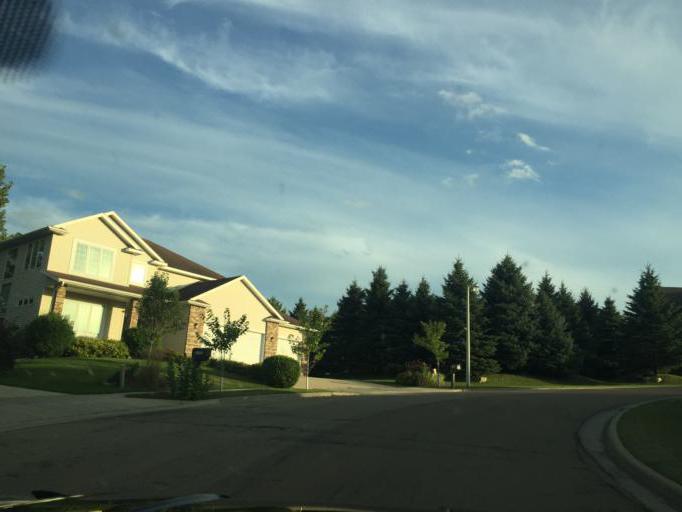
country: US
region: Minnesota
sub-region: Olmsted County
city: Rochester
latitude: 44.0161
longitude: -92.4944
